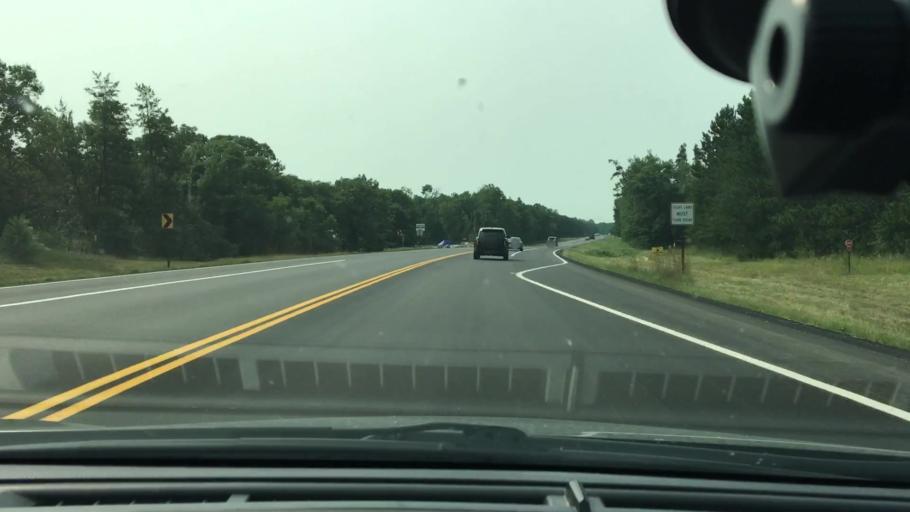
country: US
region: Minnesota
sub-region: Crow Wing County
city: Brainerd
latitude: 46.4361
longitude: -94.1718
